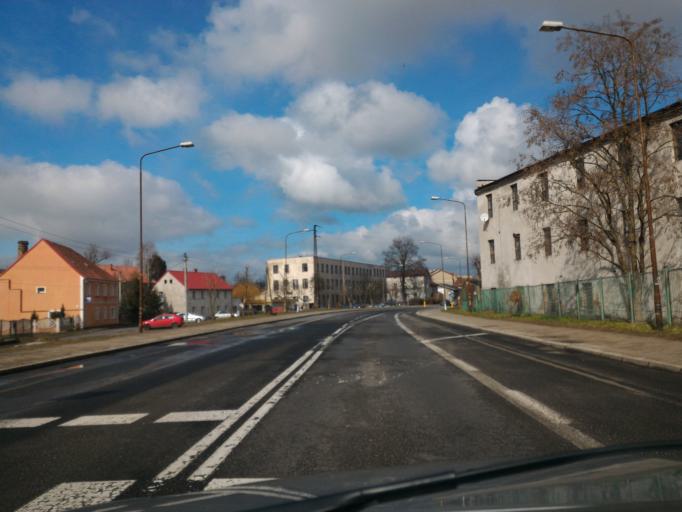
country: PL
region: Silesian Voivodeship
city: Zawidow
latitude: 51.0230
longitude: 15.0630
